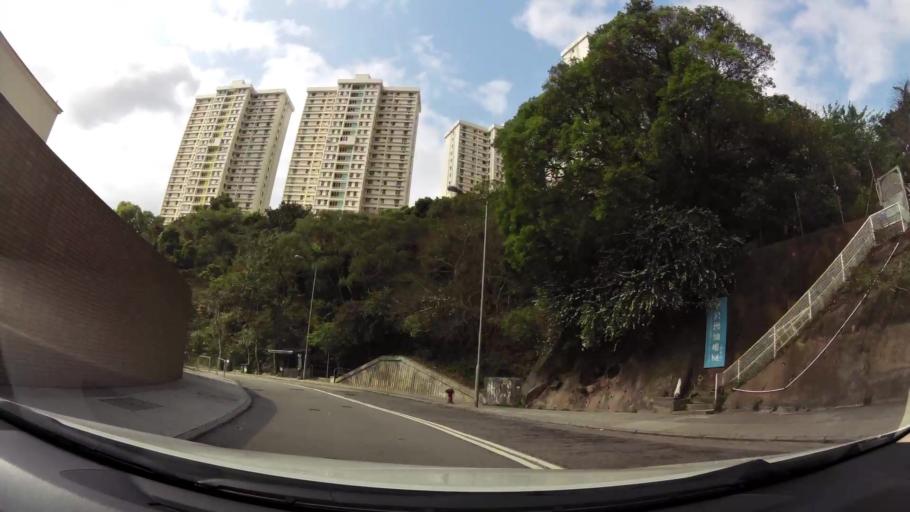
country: HK
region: Wanchai
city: Wan Chai
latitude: 22.2704
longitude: 114.1954
